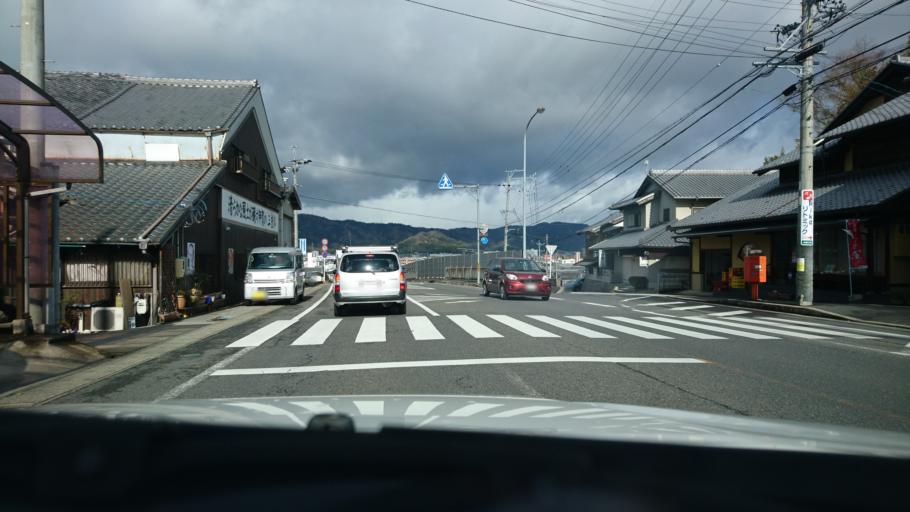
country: JP
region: Mie
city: Ueno-ebisumachi
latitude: 34.7697
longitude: 136.1235
